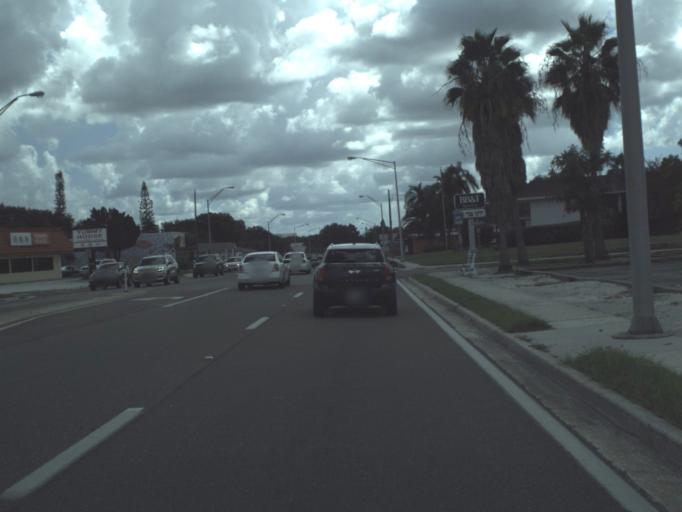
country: US
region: Florida
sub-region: Sarasota County
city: North Sarasota
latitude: 27.3651
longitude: -82.5510
